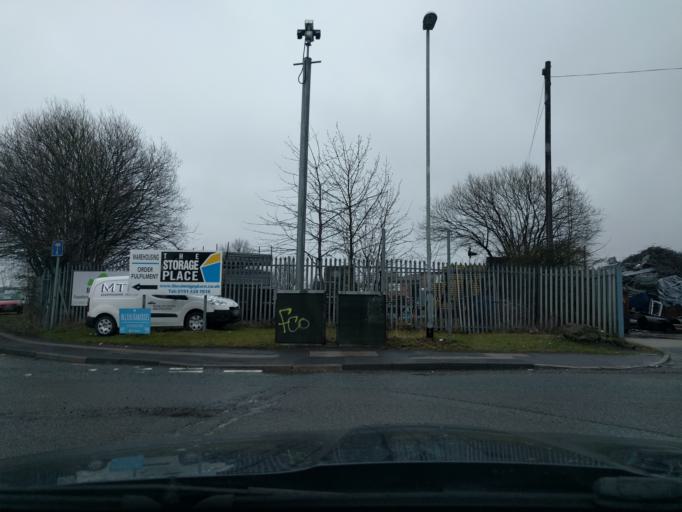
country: GB
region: England
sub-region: Gateshead
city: Felling
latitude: 54.9549
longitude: -1.5601
